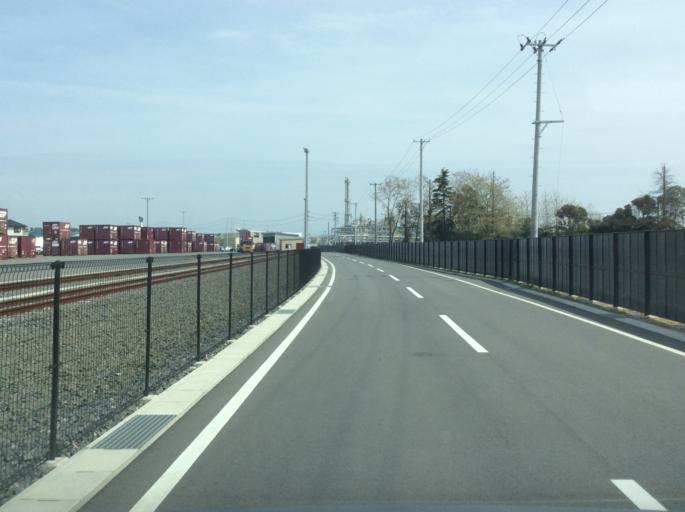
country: JP
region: Fukushima
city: Iwaki
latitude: 36.9478
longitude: 140.8967
